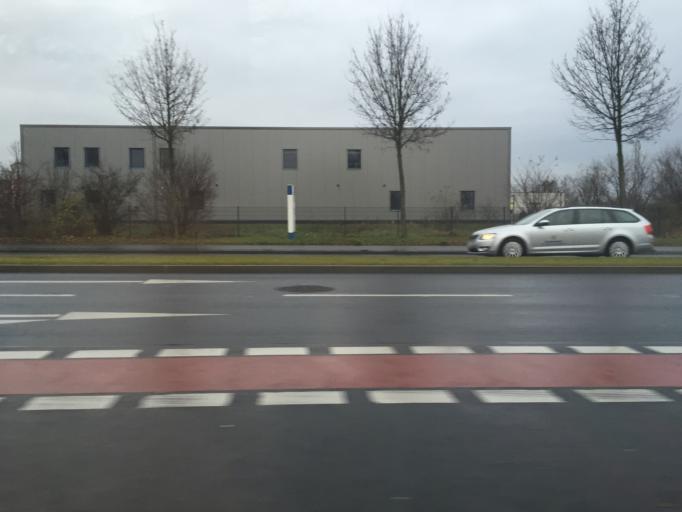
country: DE
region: Saxony
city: Albertstadt
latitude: 51.0948
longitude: 13.7668
